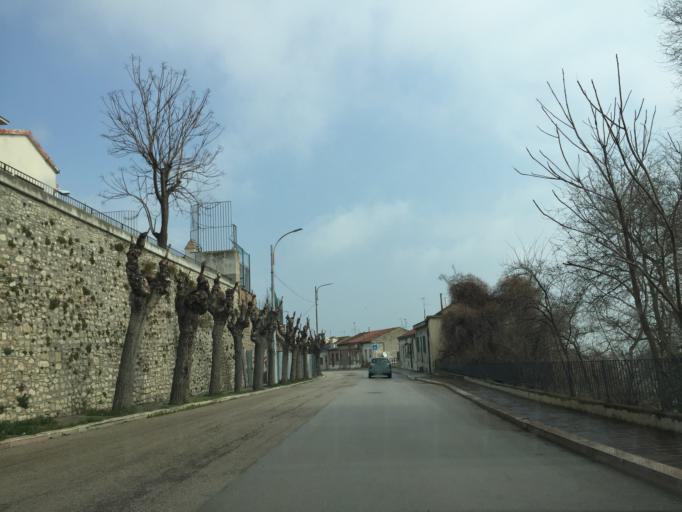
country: IT
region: Apulia
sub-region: Provincia di Foggia
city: Troia
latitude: 41.3620
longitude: 15.3123
